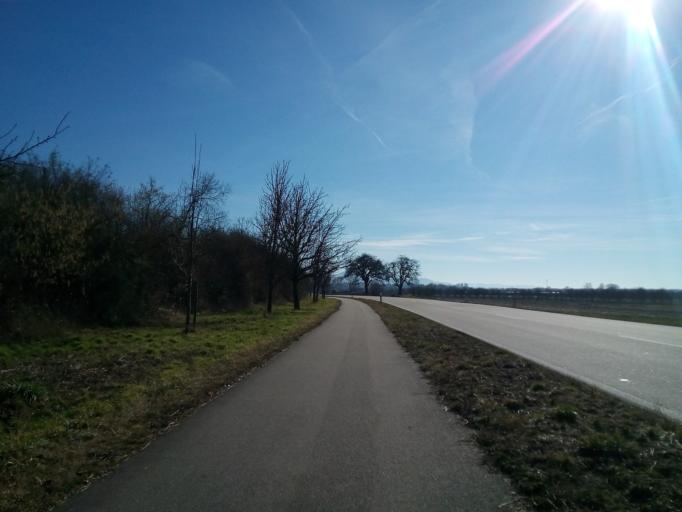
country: DE
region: Baden-Wuerttemberg
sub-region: Freiburg Region
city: Renchen
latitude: 48.6133
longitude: 8.0190
